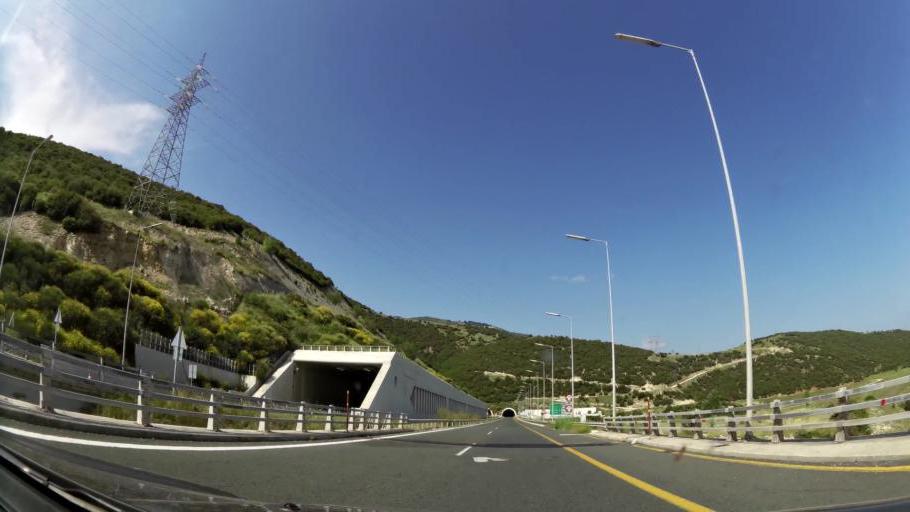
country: GR
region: West Macedonia
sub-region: Nomos Kozanis
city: Velventos
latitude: 40.3721
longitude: 22.0825
